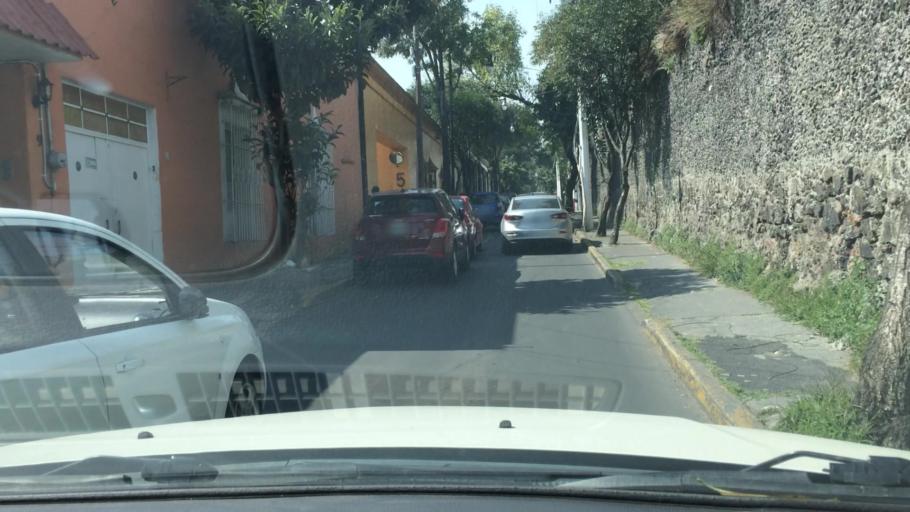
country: MX
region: Mexico City
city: Tlalpan
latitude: 19.2857
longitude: -99.1664
